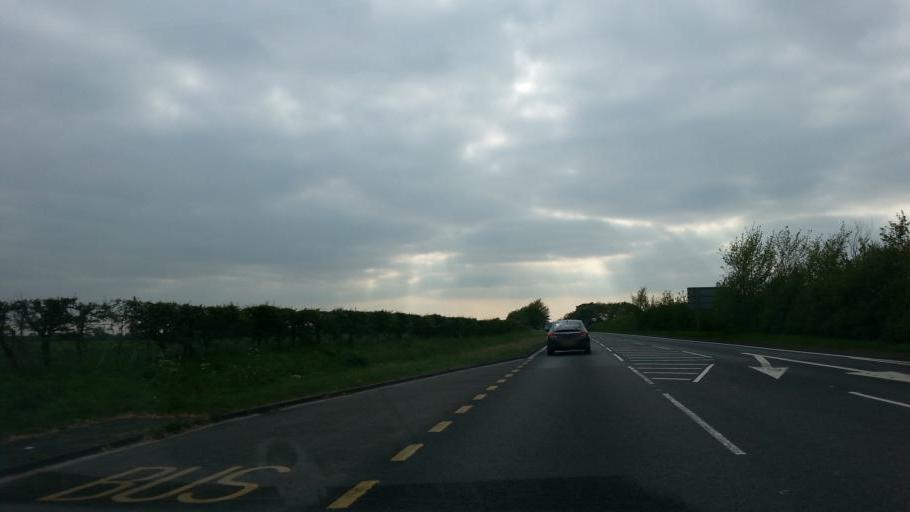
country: GB
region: England
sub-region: Lincolnshire
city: Navenby
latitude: 53.0687
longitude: -0.6364
